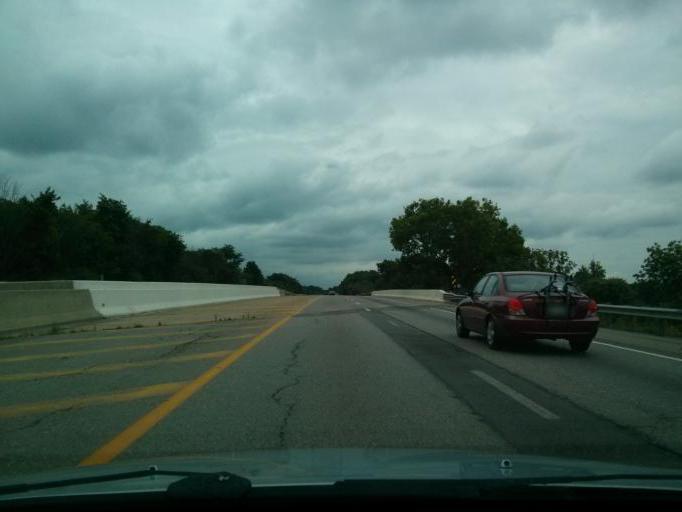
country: US
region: Ohio
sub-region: Portage County
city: Ravenna
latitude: 41.1069
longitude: -81.2181
